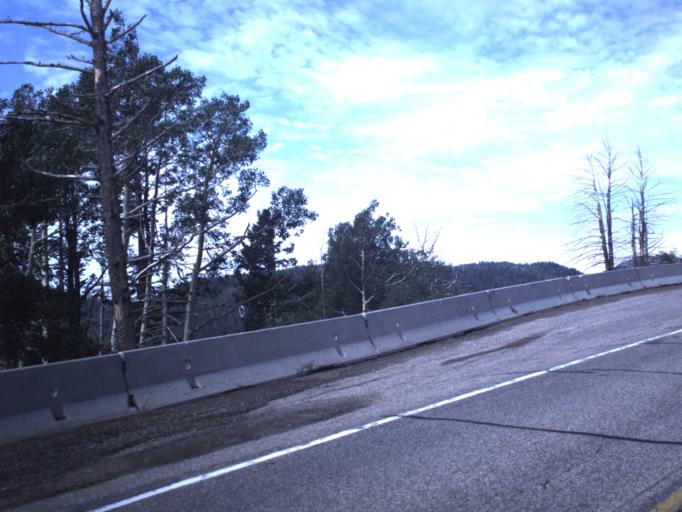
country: US
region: Utah
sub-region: Iron County
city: Parowan
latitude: 37.5269
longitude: -112.7606
